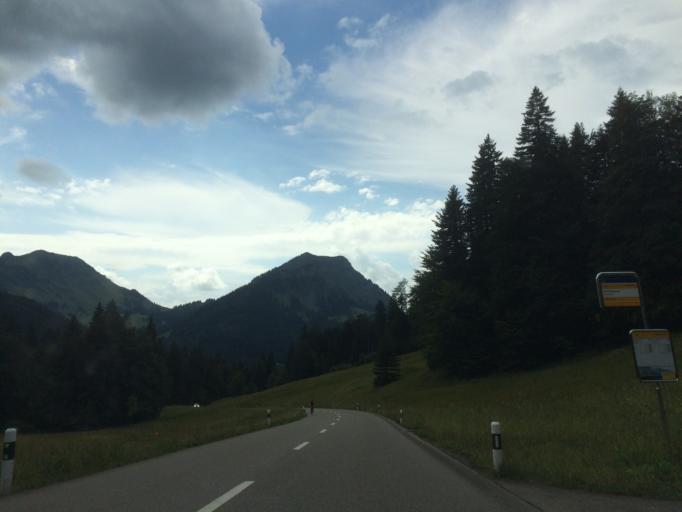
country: CH
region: Appenzell Ausserrhoden
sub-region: Bezirk Hinterland
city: Urnasch
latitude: 47.2487
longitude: 9.2840
